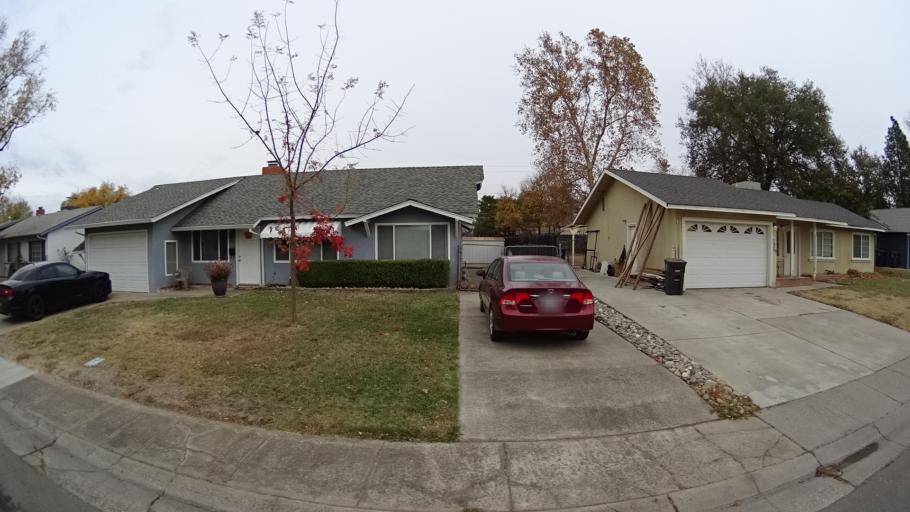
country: US
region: California
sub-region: Sacramento County
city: Citrus Heights
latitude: 38.7098
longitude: -121.2951
